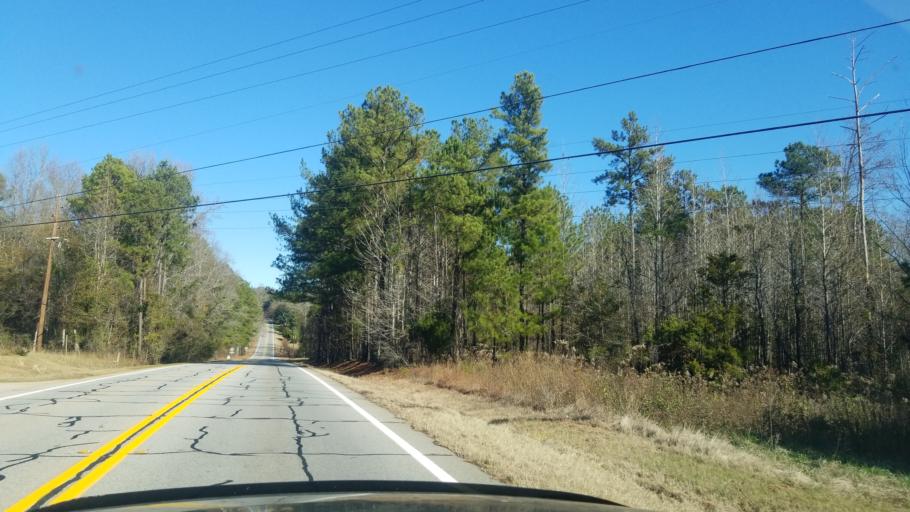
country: US
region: Georgia
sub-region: Harris County
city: Hamilton
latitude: 32.7978
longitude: -84.8678
